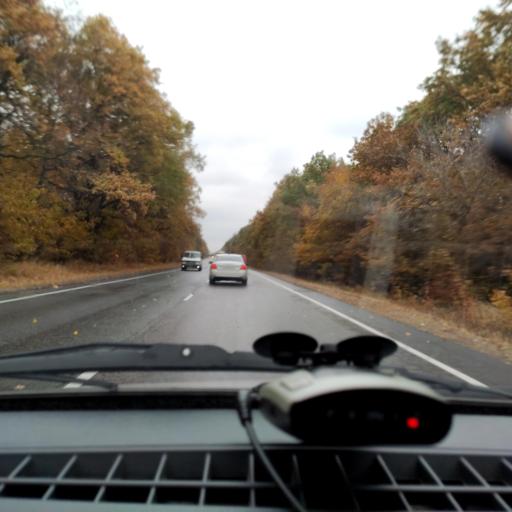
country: RU
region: Voronezj
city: Devitsa
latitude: 51.6124
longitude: 38.9814
